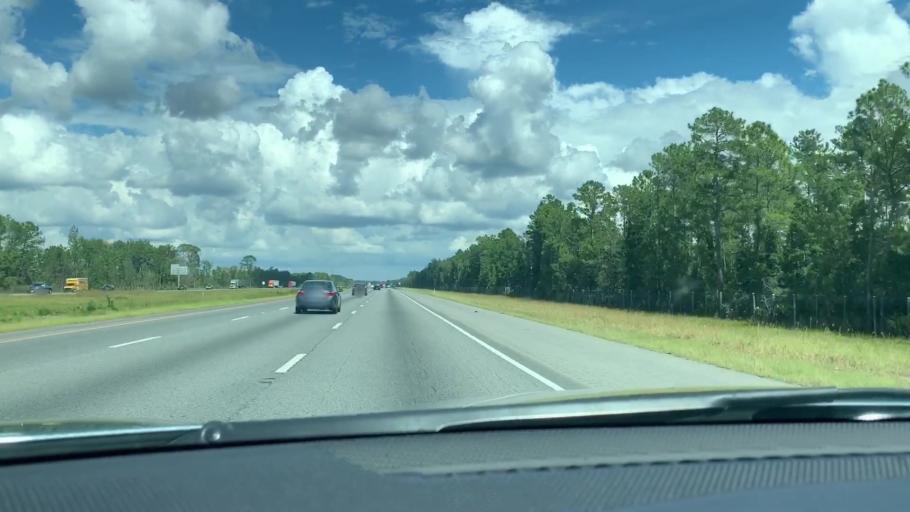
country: US
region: Georgia
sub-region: Camden County
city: Woodbine
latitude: 31.0703
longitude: -81.6248
